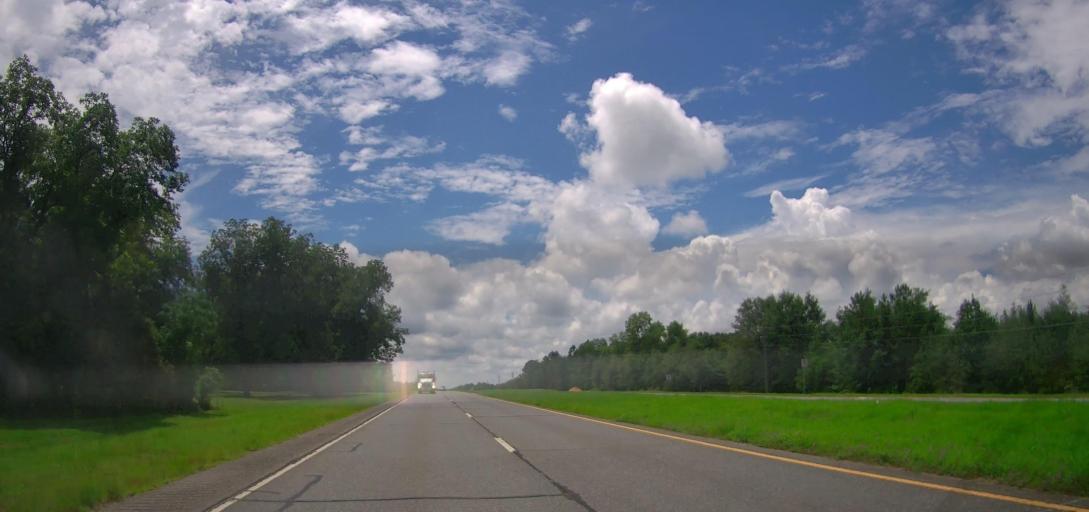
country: US
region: Georgia
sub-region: Dodge County
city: Eastman
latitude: 32.1764
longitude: -83.1726
